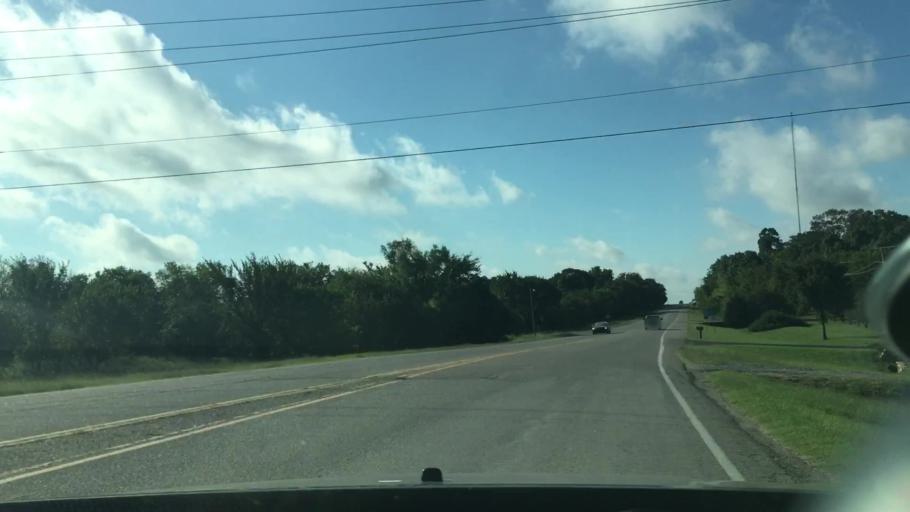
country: US
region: Oklahoma
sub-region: Bryan County
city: Durant
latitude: 34.0324
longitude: -96.3730
